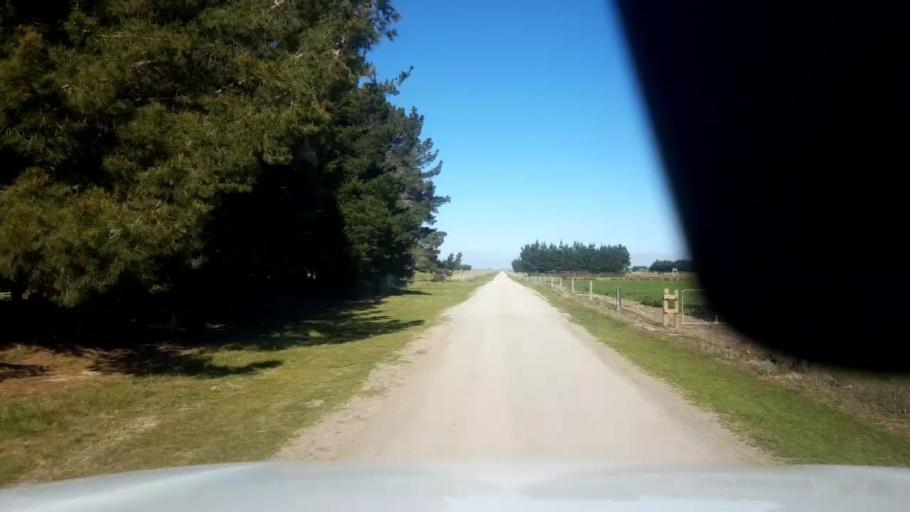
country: NZ
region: Canterbury
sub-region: Timaru District
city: Pleasant Point
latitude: -44.0684
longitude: 171.3700
